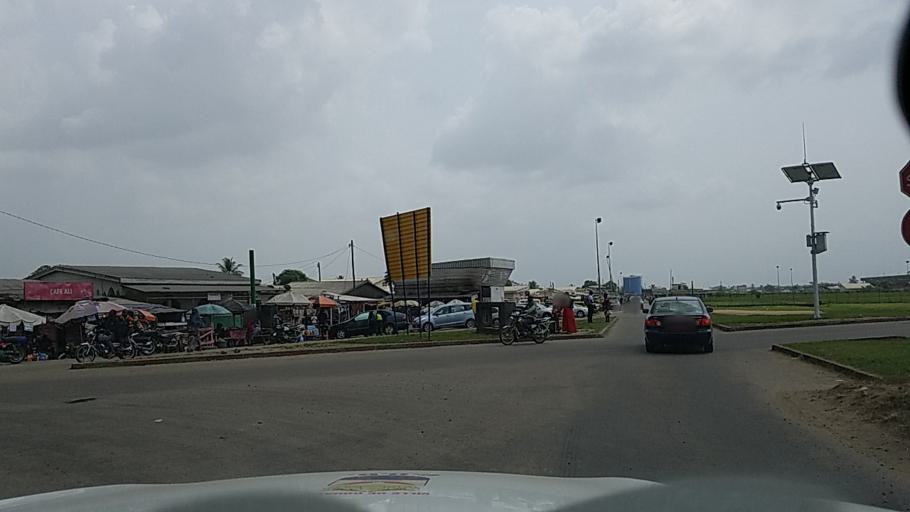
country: CM
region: Littoral
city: Douala
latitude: 4.0151
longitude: 9.7181
